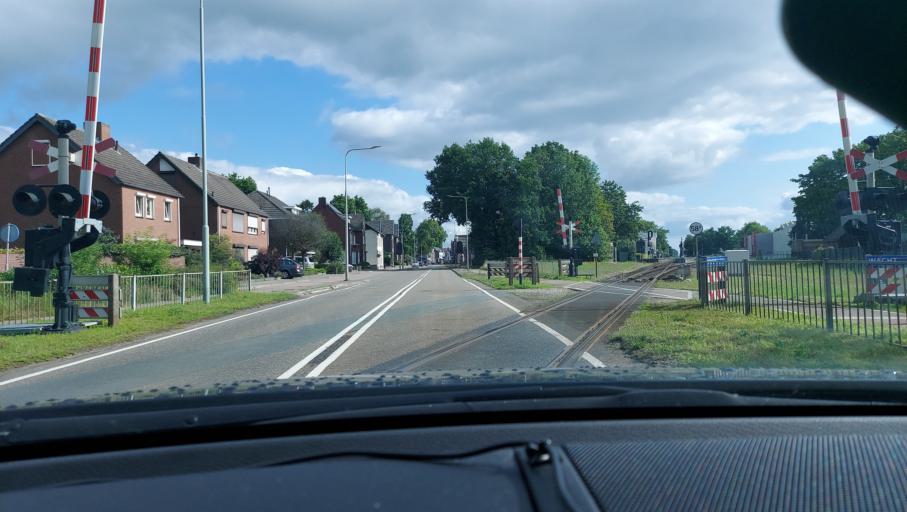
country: NL
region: Limburg
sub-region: Gemeente Beesel
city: Reuver
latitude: 51.2811
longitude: 6.0773
